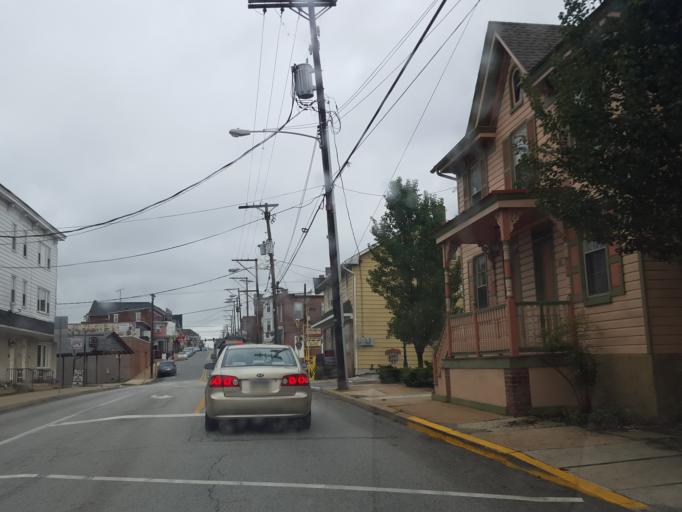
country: US
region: Pennsylvania
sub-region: York County
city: Red Lion
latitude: 39.9024
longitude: -76.6087
